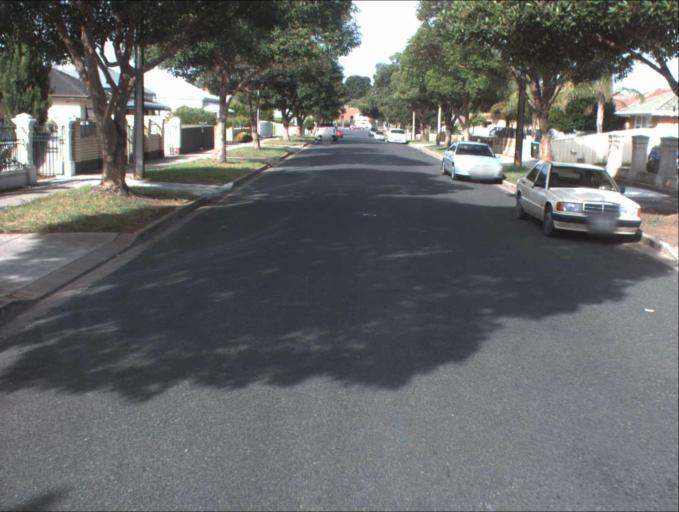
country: AU
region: South Australia
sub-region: Port Adelaide Enfield
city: Blair Athol
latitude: -34.8652
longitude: 138.5902
